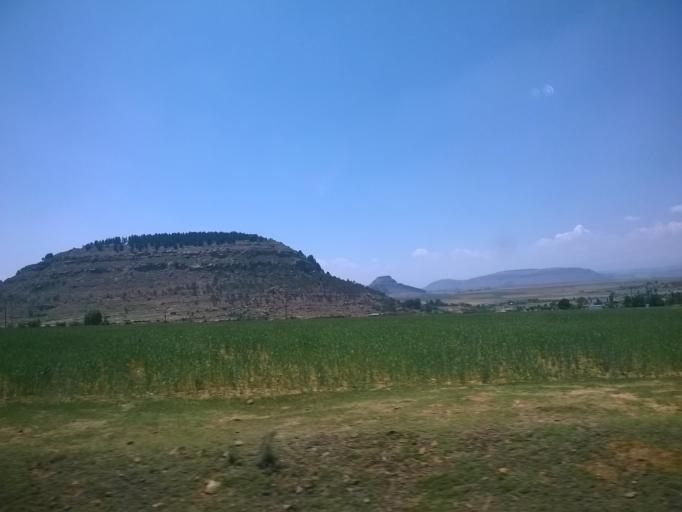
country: LS
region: Leribe
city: Maputsoe
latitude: -28.9553
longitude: 27.9610
